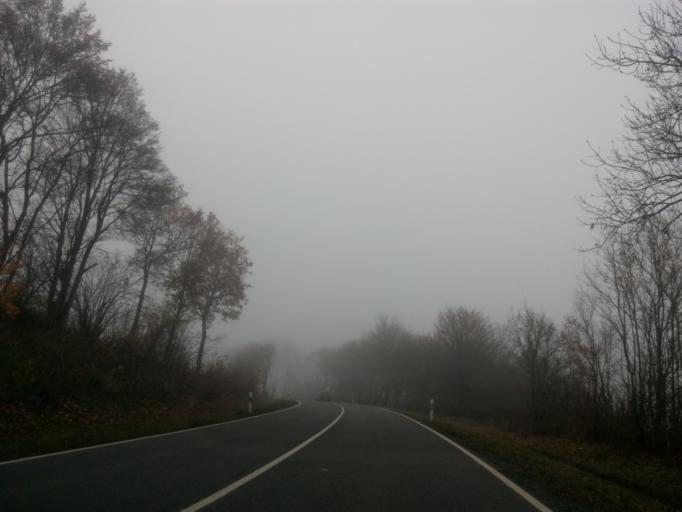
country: DE
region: Rheinland-Pfalz
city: Sien
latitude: 49.6895
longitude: 7.5154
